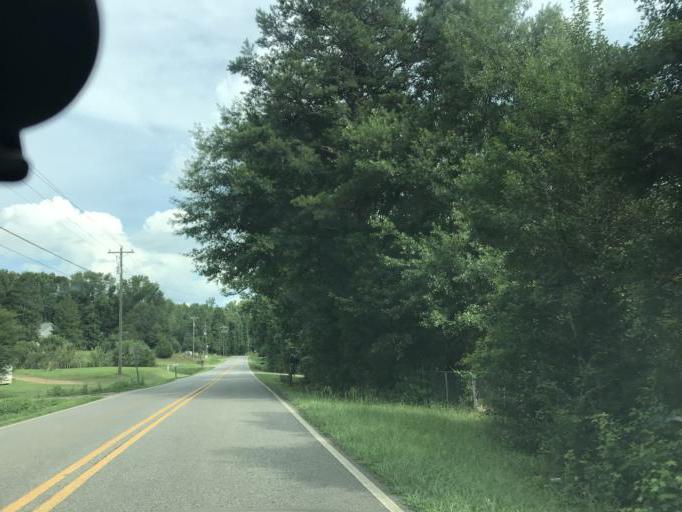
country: US
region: Georgia
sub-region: Forsyth County
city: Cumming
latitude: 34.3110
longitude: -84.1652
